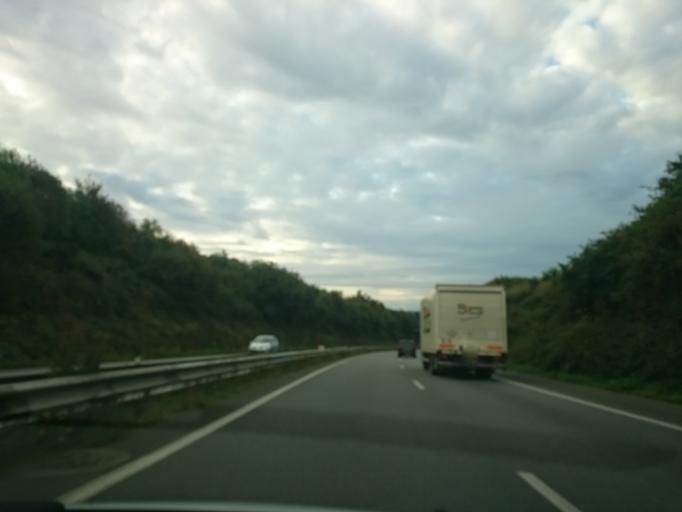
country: FR
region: Brittany
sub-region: Departement du Finistere
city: Le Relecq-Kerhuon
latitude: 48.4092
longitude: -4.4153
